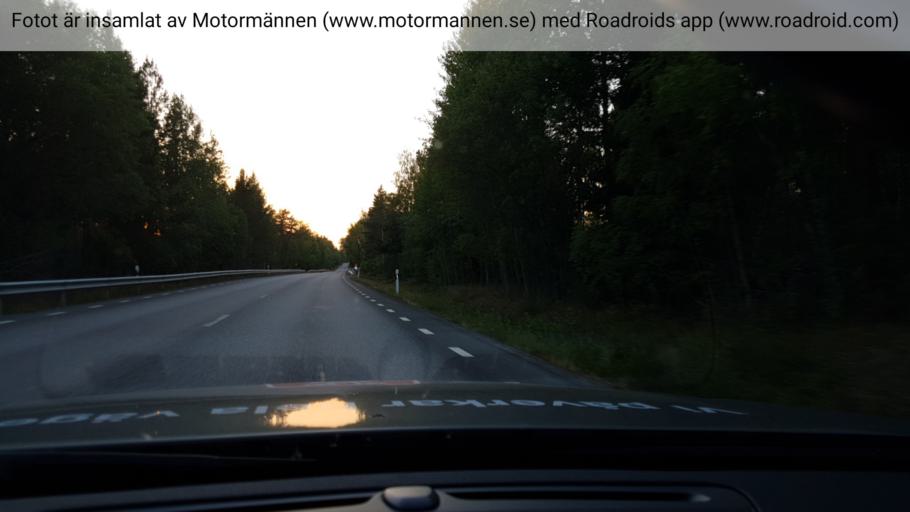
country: SE
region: Uppsala
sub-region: Osthammars Kommun
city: Bjorklinge
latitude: 59.9833
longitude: 17.3330
